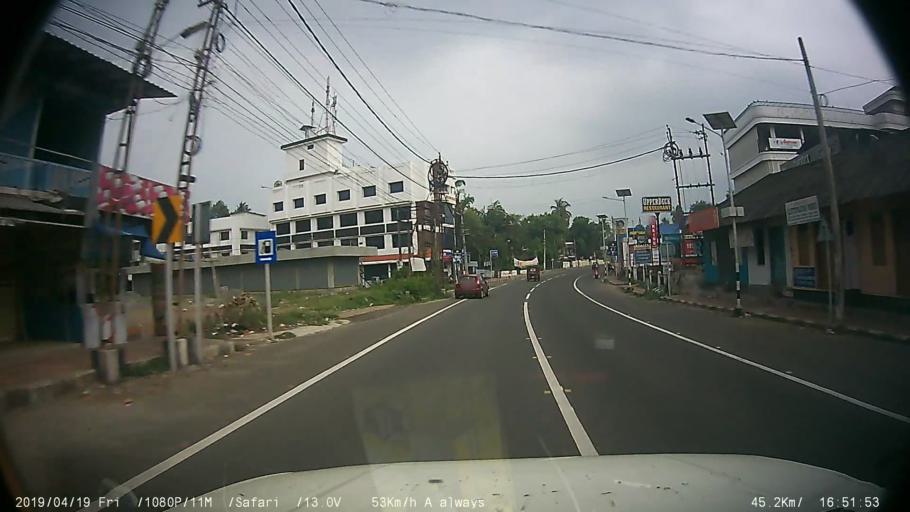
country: IN
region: Kerala
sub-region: Kottayam
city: Changanacheri
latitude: 9.4548
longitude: 76.5358
